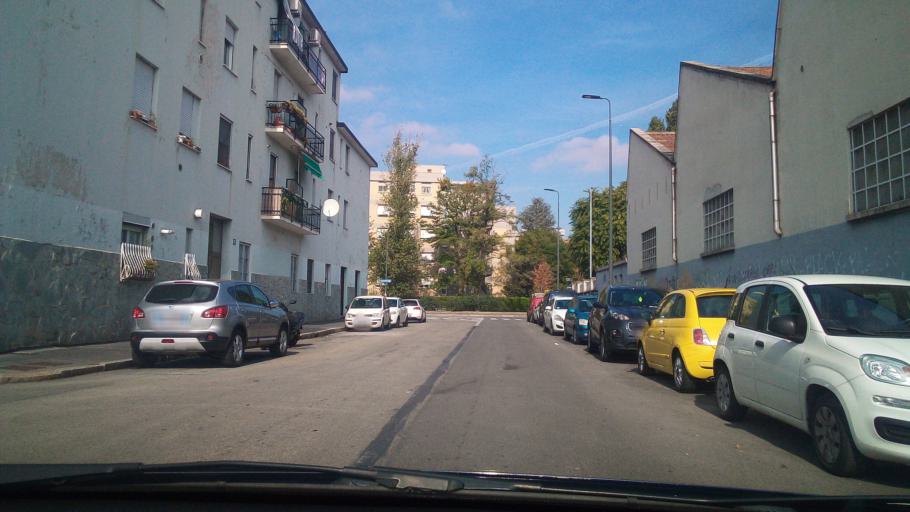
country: IT
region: Lombardy
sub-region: Citta metropolitana di Milano
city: Sesto San Giovanni
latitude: 45.5101
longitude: 9.2299
